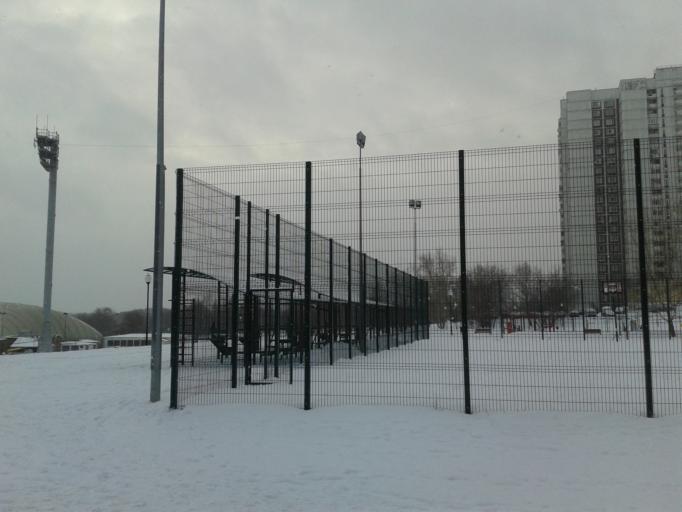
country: RU
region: Moscow
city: Strogino
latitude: 55.8019
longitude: 37.4130
